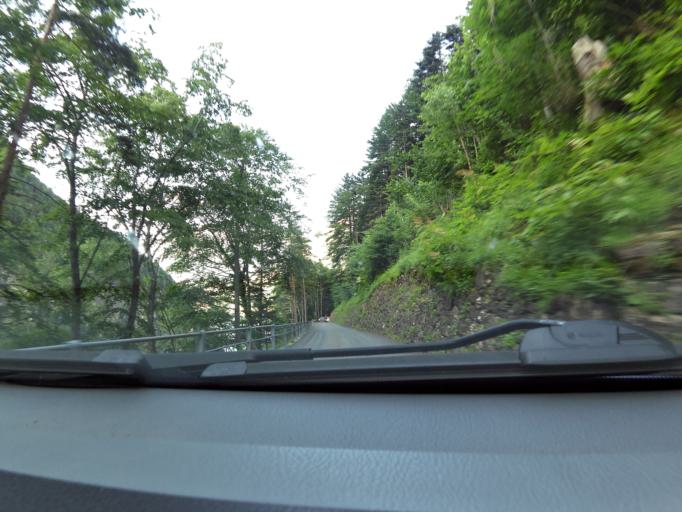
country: CH
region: Uri
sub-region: Uri
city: Bauen
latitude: 46.9144
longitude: 8.5864
